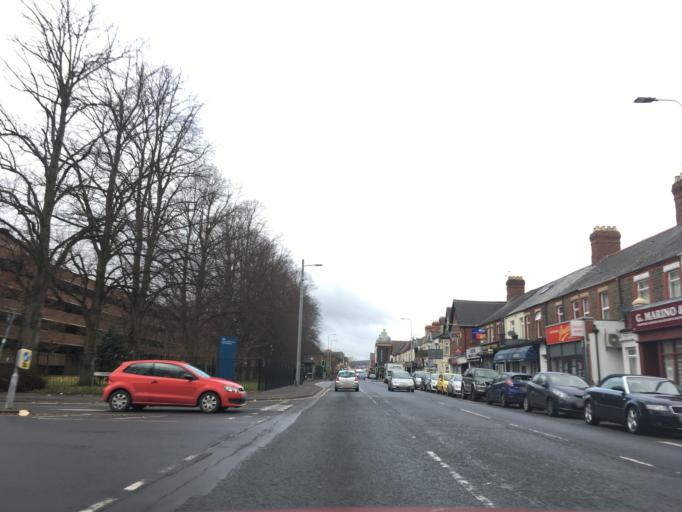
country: GB
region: Wales
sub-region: Cardiff
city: Cardiff
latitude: 51.5000
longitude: -3.1864
